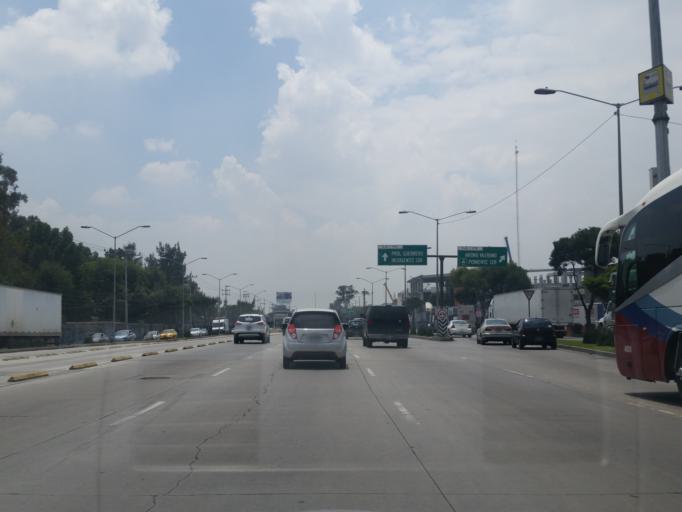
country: MX
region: Mexico
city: Colonia Lindavista
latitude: 19.4915
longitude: -99.1529
